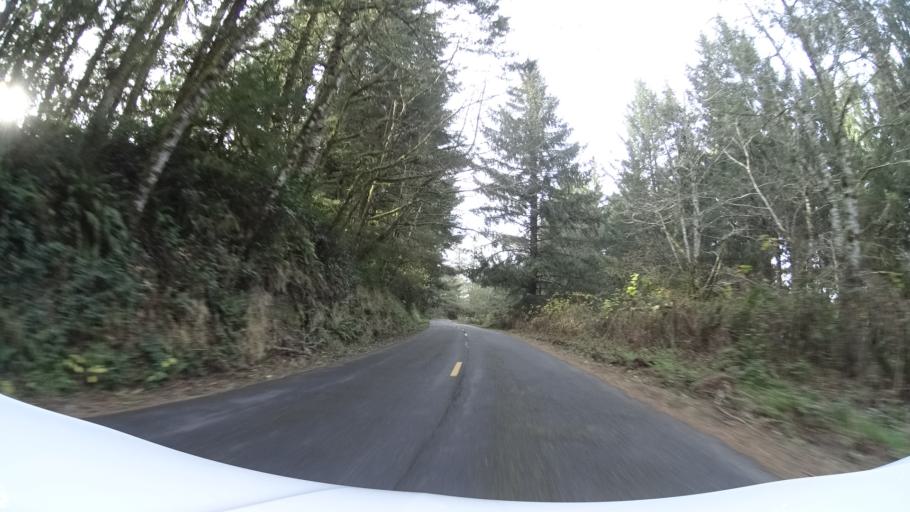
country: US
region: California
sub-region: Humboldt County
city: Ferndale
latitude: 40.5351
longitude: -124.2721
